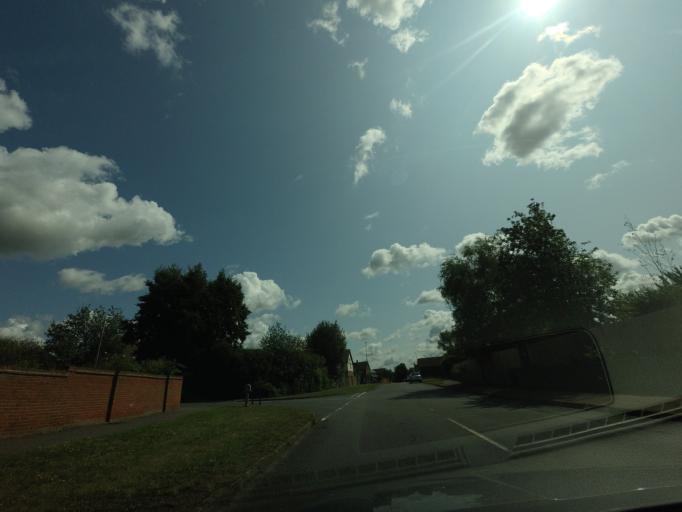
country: GB
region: England
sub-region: Kent
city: Boxley
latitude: 51.2722
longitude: 0.5520
